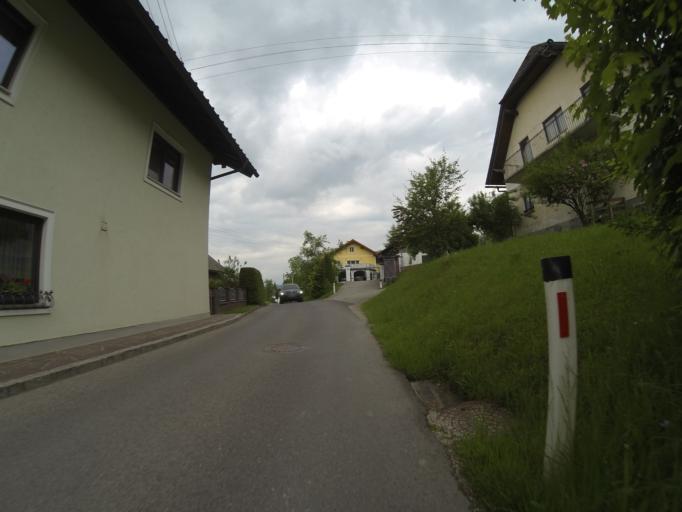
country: AT
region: Upper Austria
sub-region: Politischer Bezirk Gmunden
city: Altmunster
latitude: 47.9285
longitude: 13.7654
